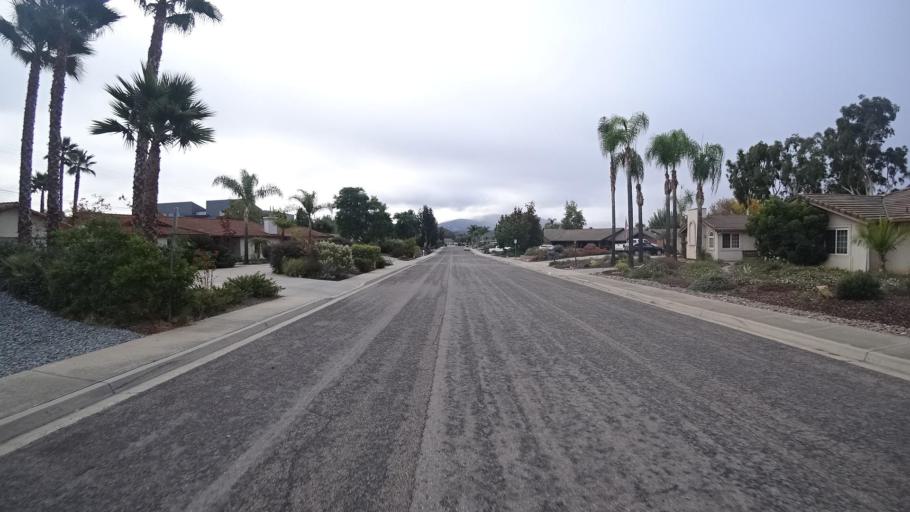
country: US
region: California
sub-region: San Diego County
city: Rancho San Diego
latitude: 32.7607
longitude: -116.9230
